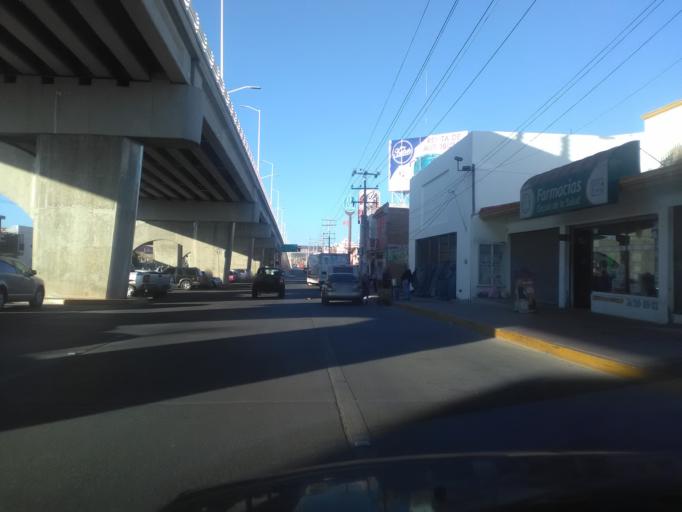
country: MX
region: Durango
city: Victoria de Durango
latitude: 24.0097
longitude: -104.6929
